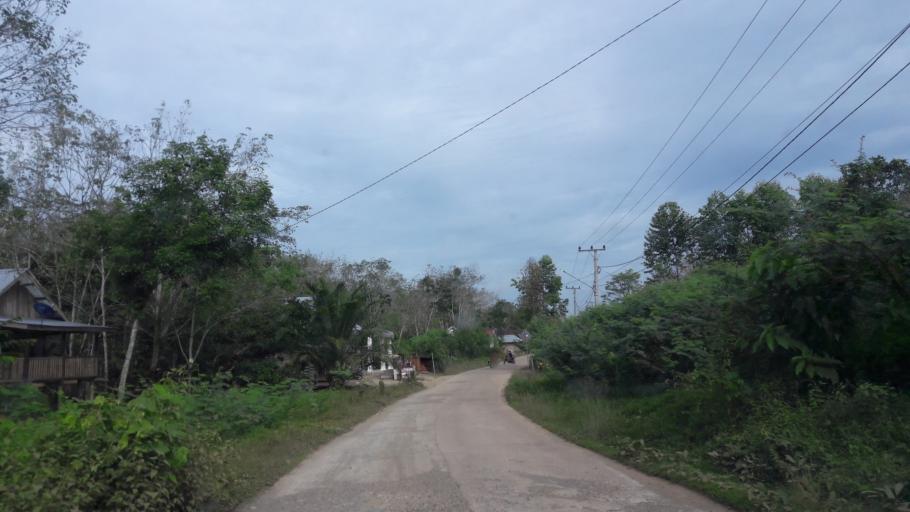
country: ID
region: South Sumatra
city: Gunungmegang Dalam
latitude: -3.2869
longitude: 103.7220
